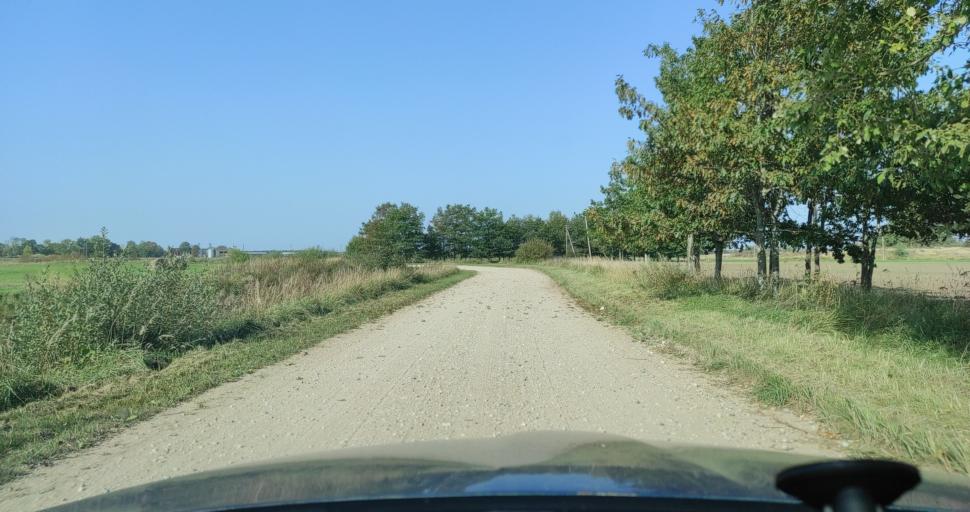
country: LV
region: Ventspils Rajons
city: Piltene
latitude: 57.2323
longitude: 21.6102
